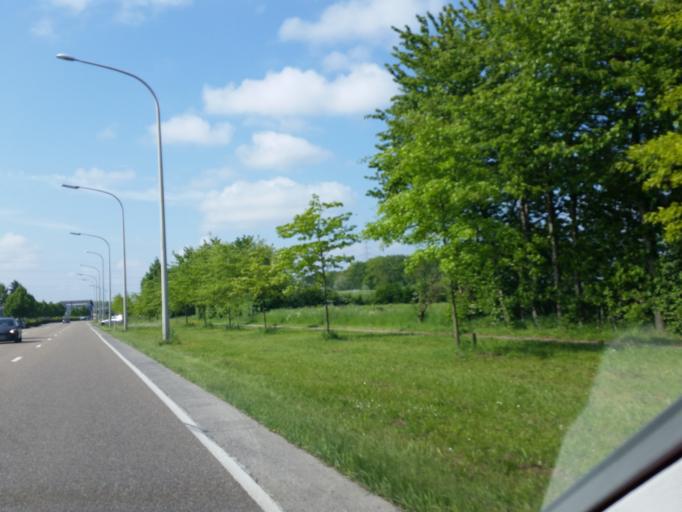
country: BE
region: Flanders
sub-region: Provincie Vlaams-Brabant
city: Zemst
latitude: 50.9579
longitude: 4.4555
